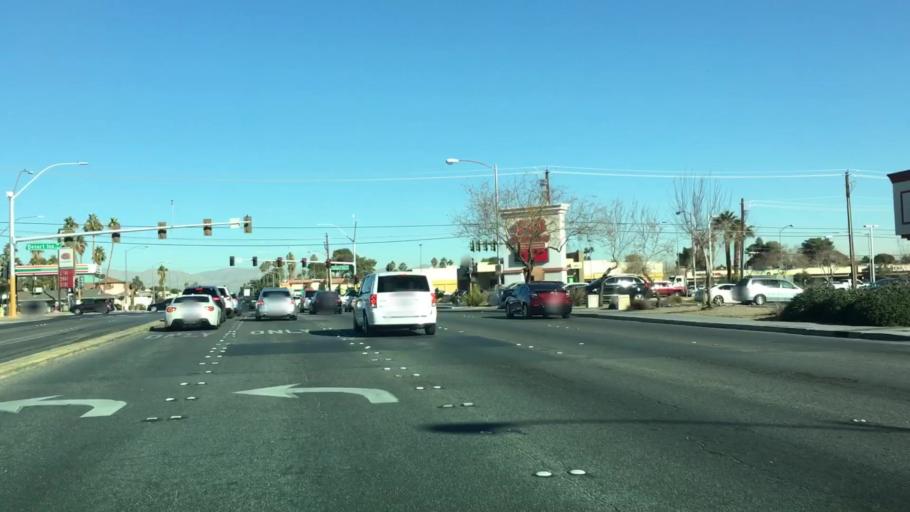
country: US
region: Nevada
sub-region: Clark County
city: Winchester
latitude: 36.1290
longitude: -115.1186
